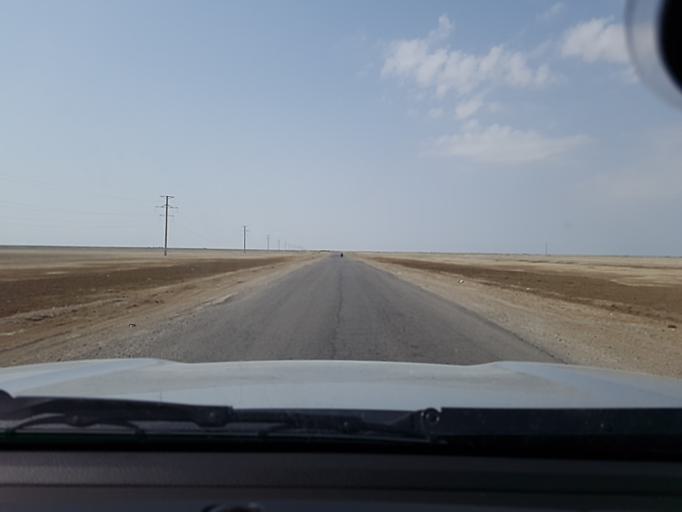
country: TM
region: Balkan
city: Gumdag
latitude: 39.0524
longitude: 54.5841
